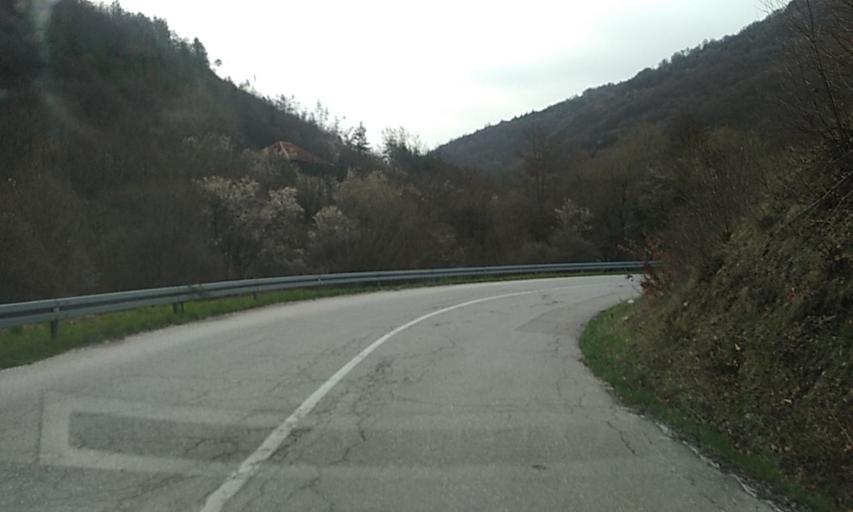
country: RS
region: Central Serbia
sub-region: Pcinjski Okrug
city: Bosilegrad
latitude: 42.5319
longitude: 22.4257
